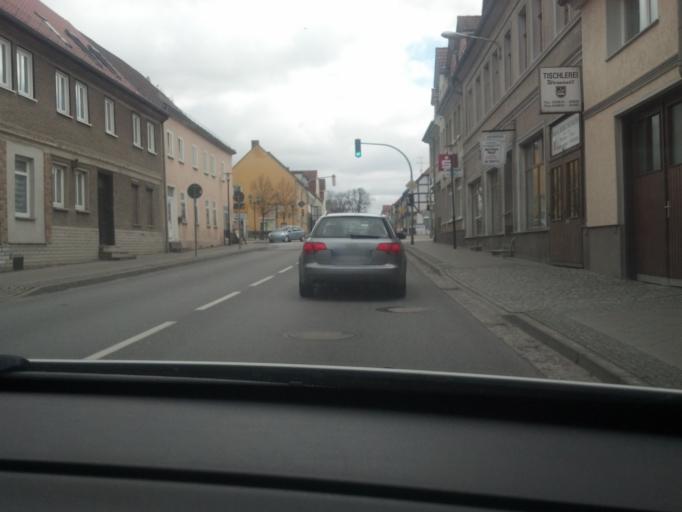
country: DE
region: Mecklenburg-Vorpommern
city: Rechlin
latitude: 53.2748
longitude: 12.8144
